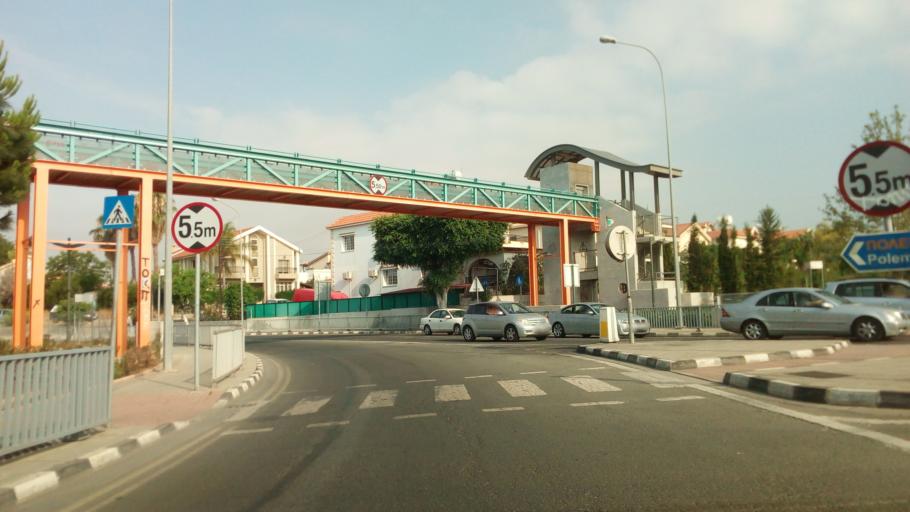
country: CY
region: Limassol
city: Pano Polemidia
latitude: 34.6941
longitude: 33.0130
